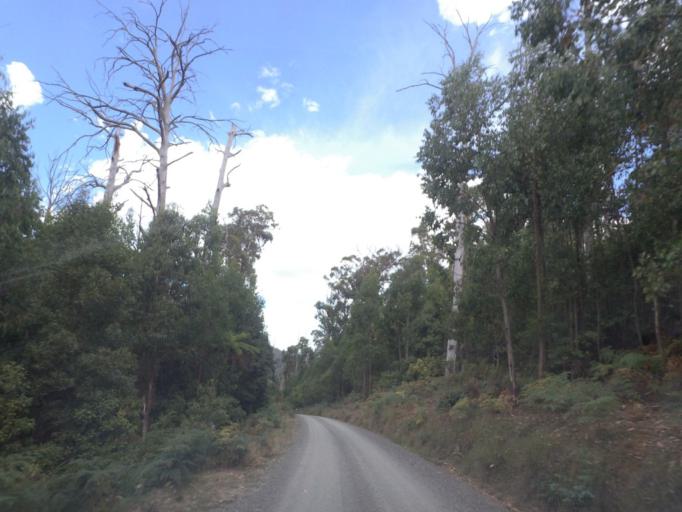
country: AU
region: Victoria
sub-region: Murrindindi
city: Alexandra
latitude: -37.4116
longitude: 145.7575
